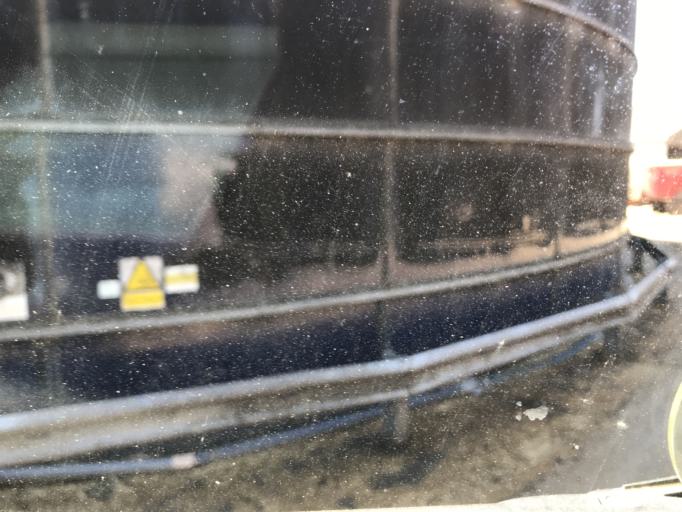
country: GB
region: England
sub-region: Cheshire East
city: Nantwich
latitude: 53.1044
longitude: -2.5384
